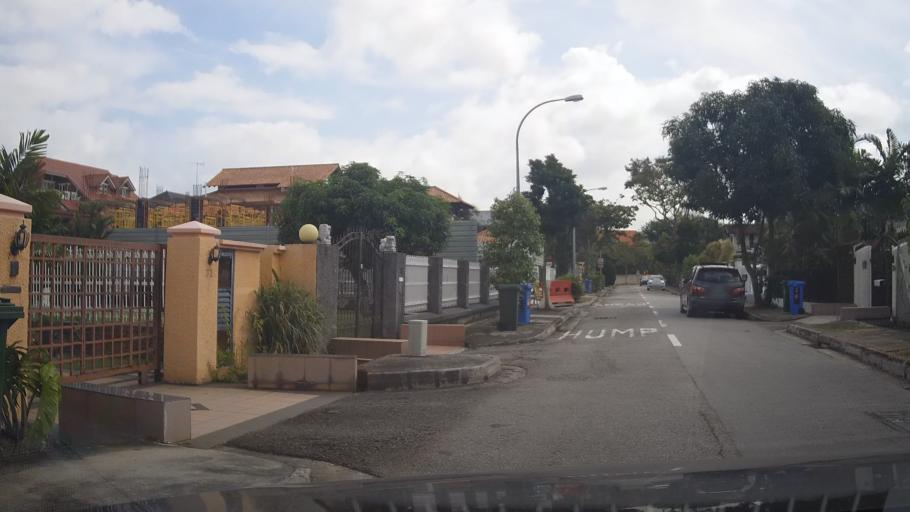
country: SG
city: Singapore
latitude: 1.3154
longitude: 103.9166
